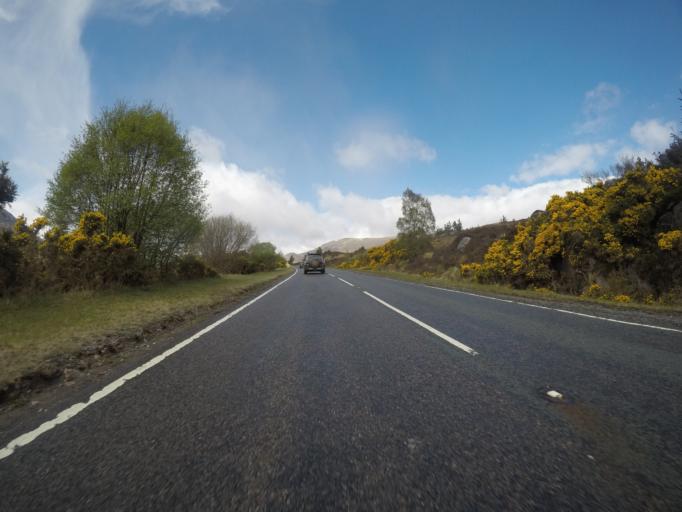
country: GB
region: Scotland
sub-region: Highland
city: Spean Bridge
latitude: 57.1464
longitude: -4.9979
